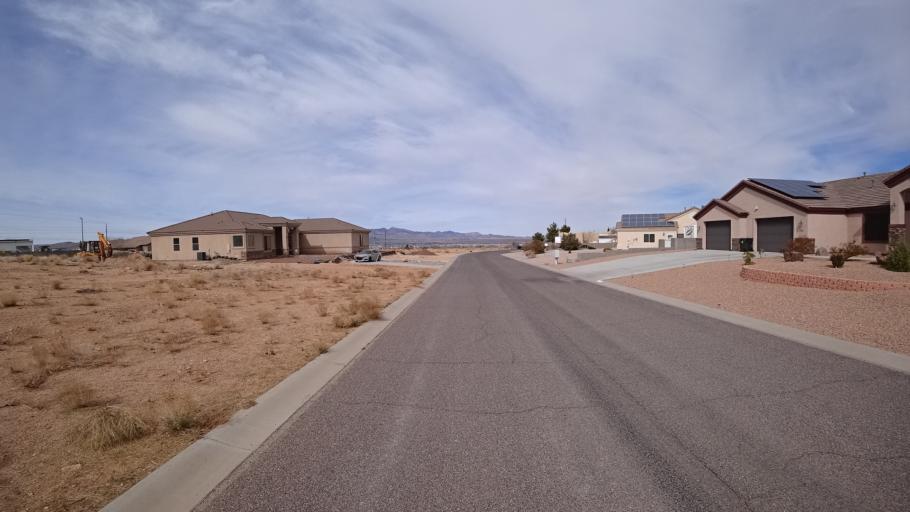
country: US
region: Arizona
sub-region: Mohave County
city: Kingman
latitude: 35.1945
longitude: -113.9842
